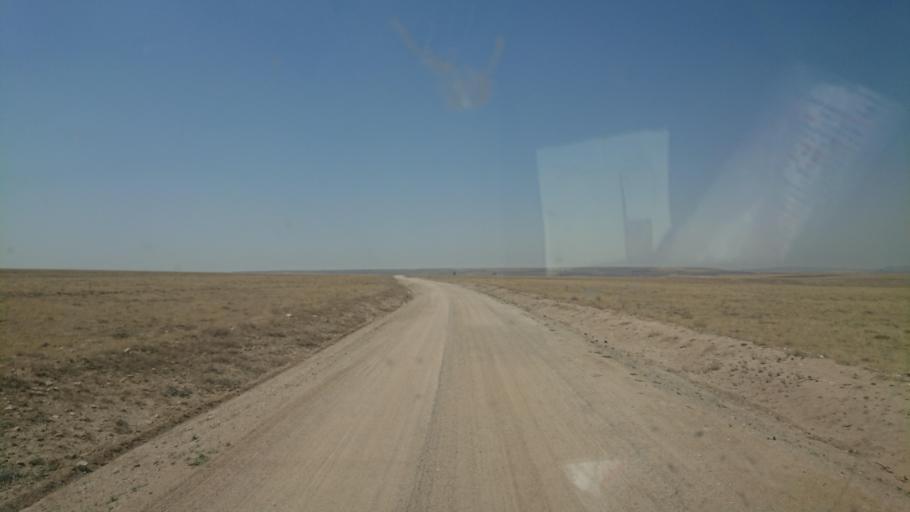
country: TR
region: Aksaray
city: Agacoren
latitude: 38.7428
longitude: 33.8885
